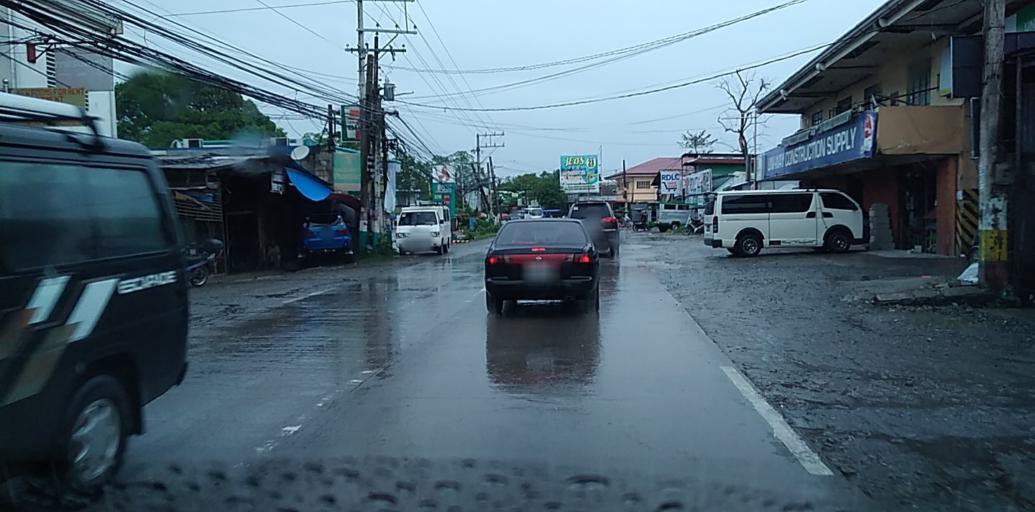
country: PH
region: Central Luzon
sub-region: Province of Pampanga
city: Mexico
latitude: 15.0605
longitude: 120.7193
